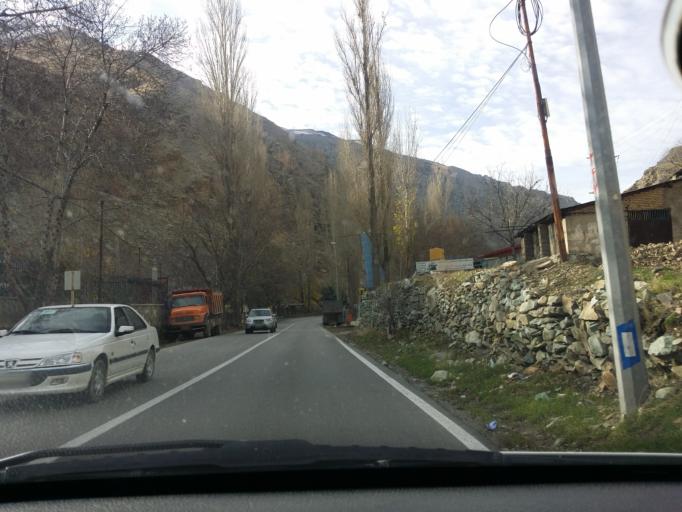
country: IR
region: Alborz
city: Karaj
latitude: 36.0172
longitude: 51.1475
